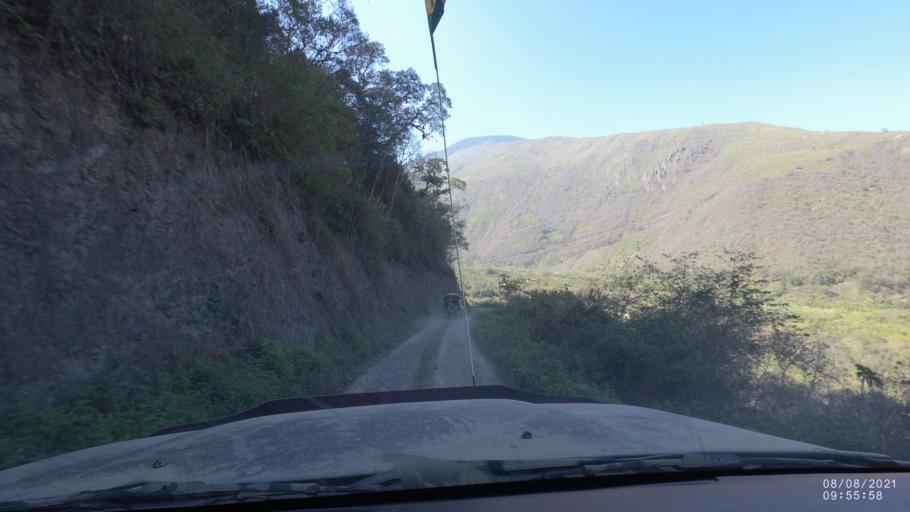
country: BO
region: La Paz
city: Quime
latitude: -16.6361
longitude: -66.7275
